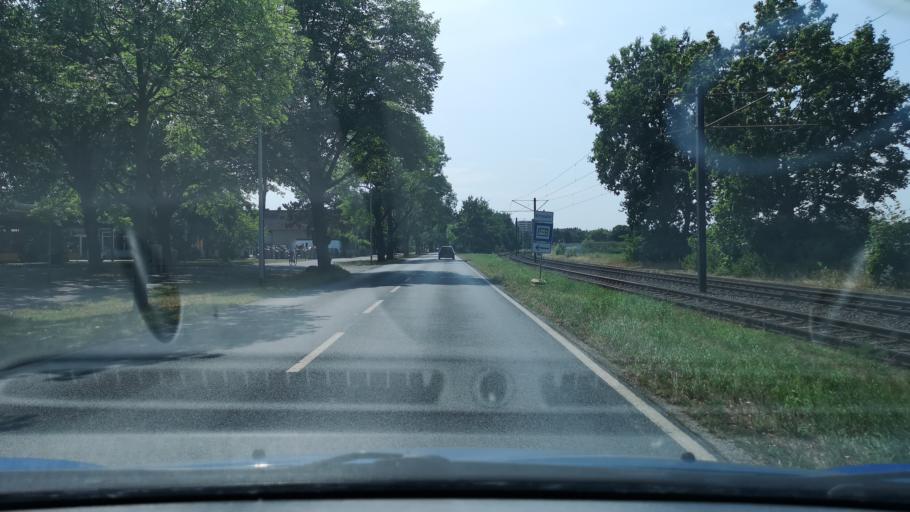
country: DE
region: Lower Saxony
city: Isernhagen Farster Bauerschaft
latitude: 52.4243
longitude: 9.7995
